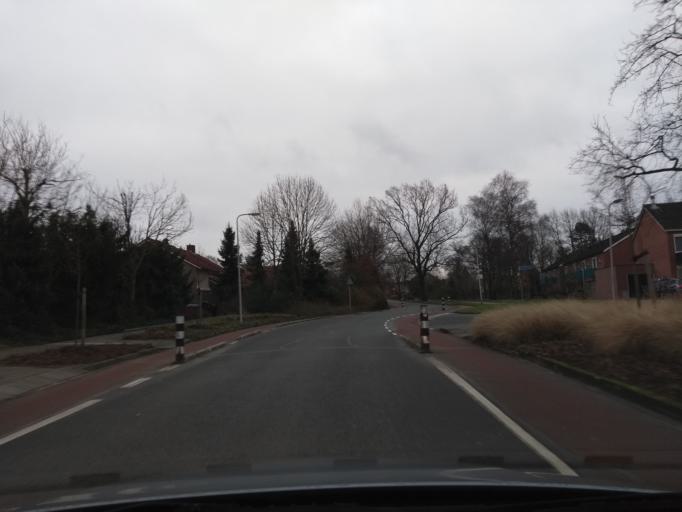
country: NL
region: Overijssel
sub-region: Gemeente Haaksbergen
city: Haaksbergen
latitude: 52.1664
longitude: 6.7503
